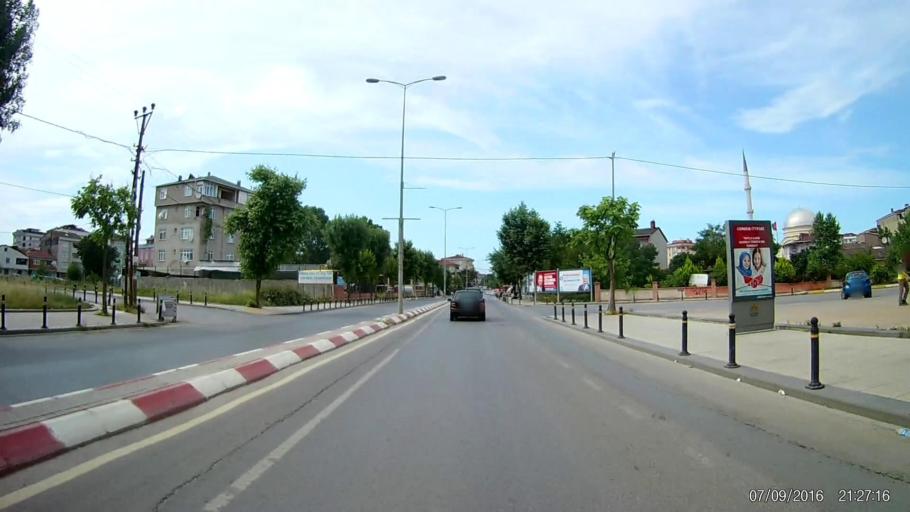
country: TR
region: Istanbul
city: Sultanbeyli
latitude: 40.9853
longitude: 29.2645
